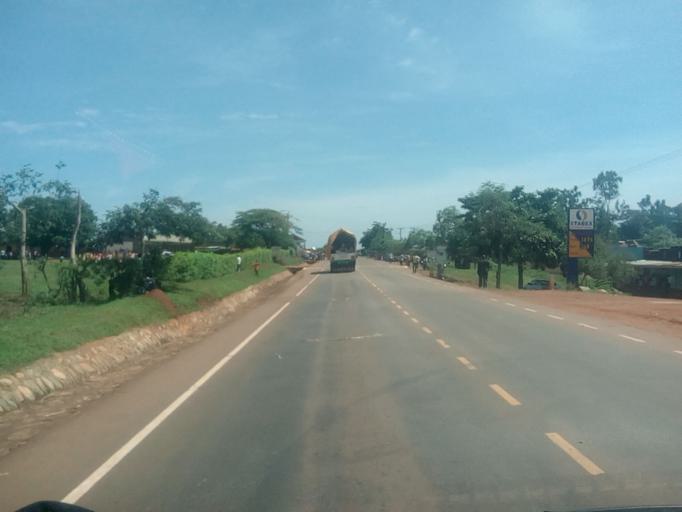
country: UG
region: Eastern Region
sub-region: Jinja District
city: Buwenge
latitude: 0.7003
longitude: 33.1595
